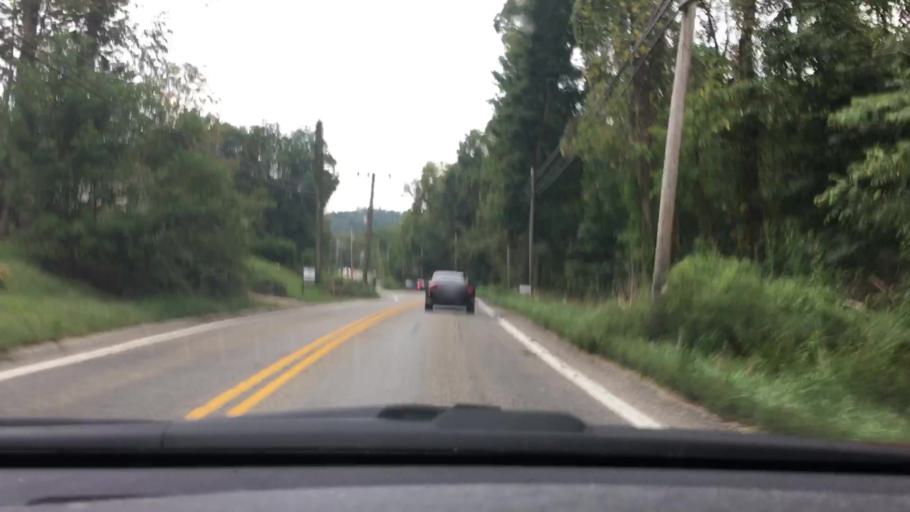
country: US
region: Pennsylvania
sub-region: Allegheny County
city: Baldwin
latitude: 40.3323
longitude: -79.9980
